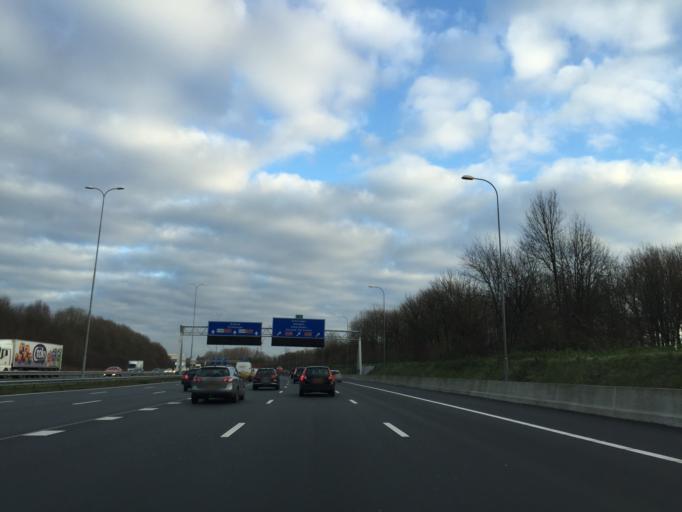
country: NL
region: Utrecht
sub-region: Gemeente Utrecht
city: Lunetten
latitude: 52.0754
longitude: 5.1564
